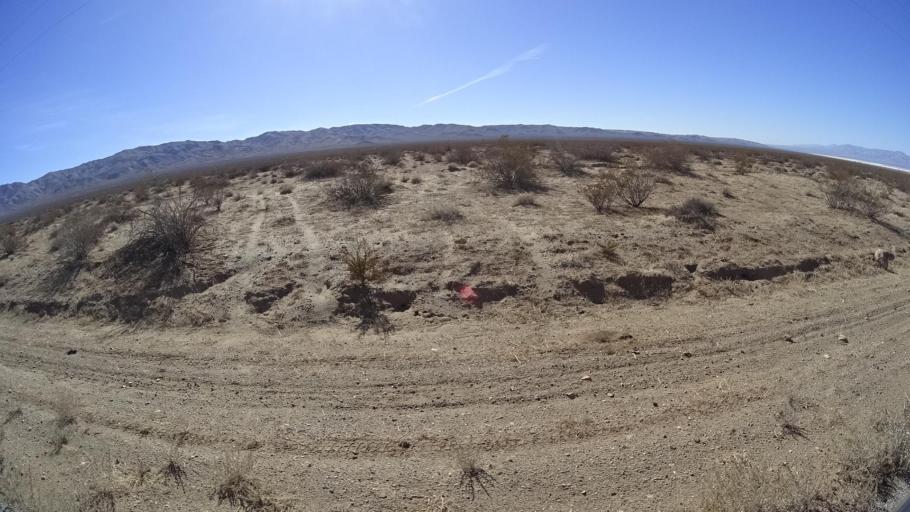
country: US
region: California
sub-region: Kern County
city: Ridgecrest
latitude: 35.3857
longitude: -117.7309
